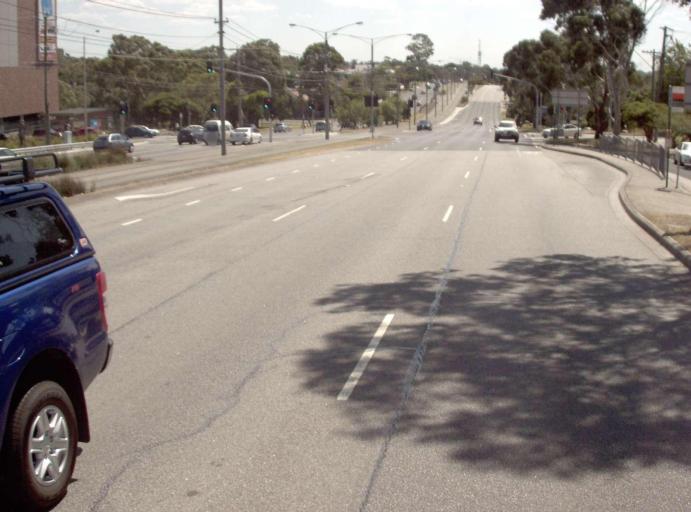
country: AU
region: Victoria
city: Burwood East
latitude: -37.8522
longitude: 145.1498
